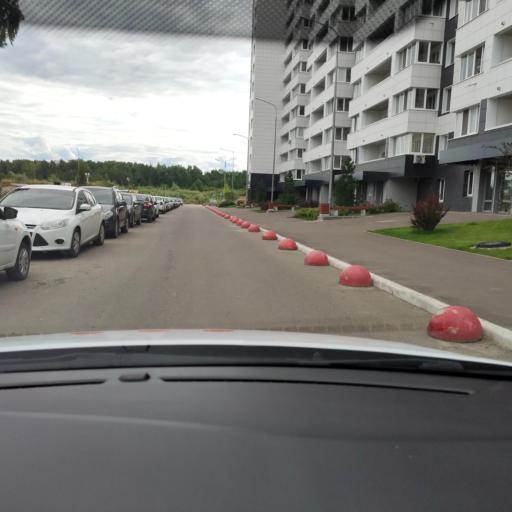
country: RU
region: Tatarstan
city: Osinovo
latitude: 55.8455
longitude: 48.9073
